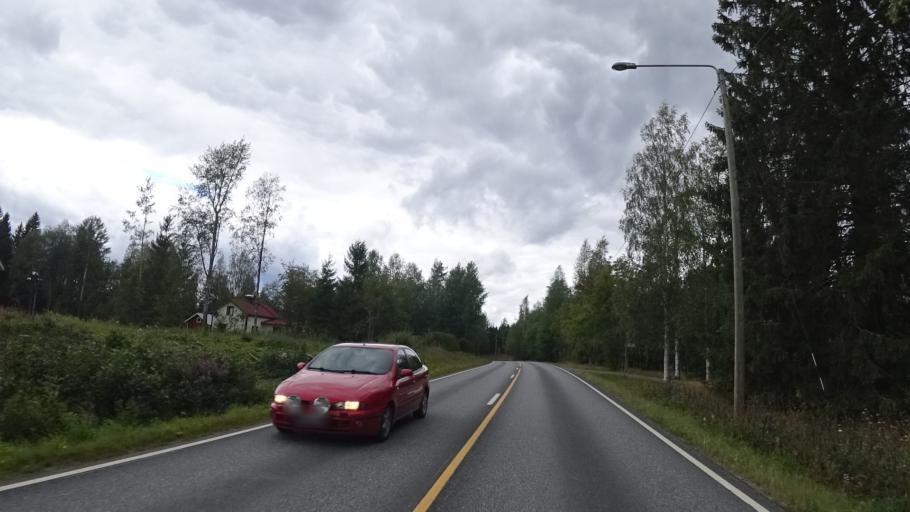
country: FI
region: North Karelia
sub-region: Joensuu
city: Ilomantsi
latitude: 62.6517
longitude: 30.9708
